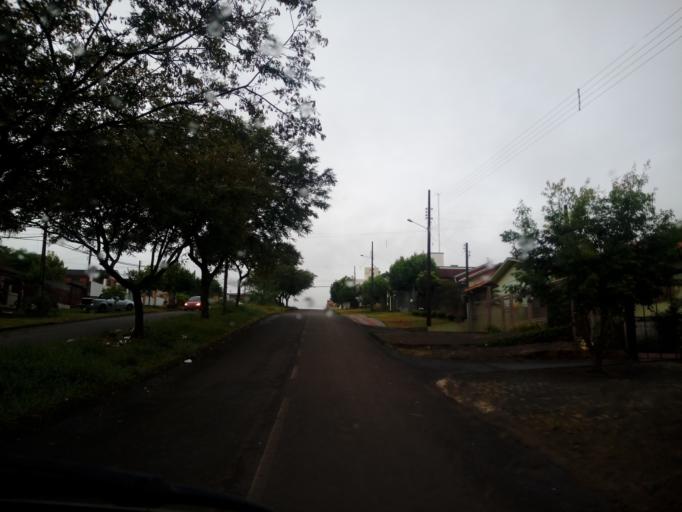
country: BR
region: Santa Catarina
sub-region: Chapeco
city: Chapeco
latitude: -27.0810
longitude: -52.6054
